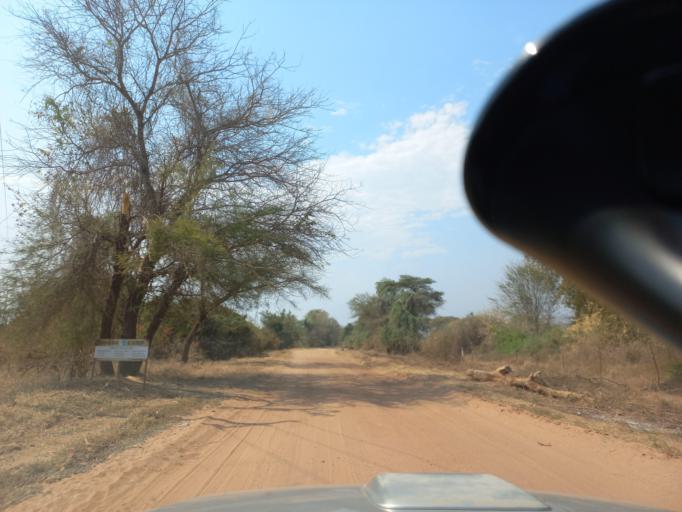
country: ZW
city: Chirundu
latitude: -15.9312
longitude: 28.8713
